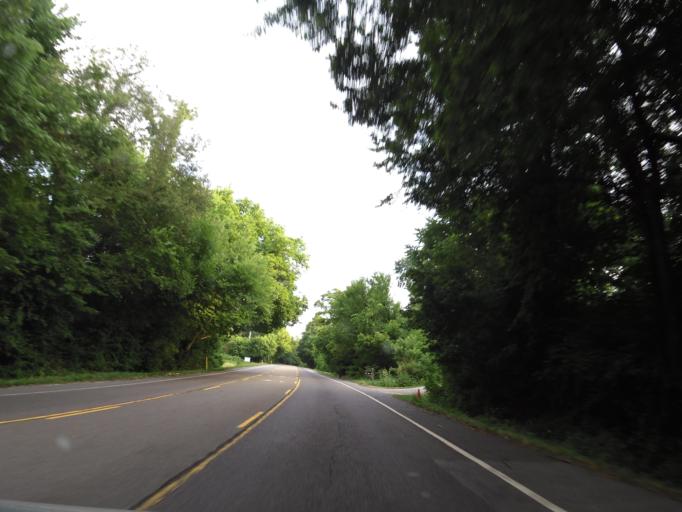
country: US
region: Tennessee
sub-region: Knox County
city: Knoxville
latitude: 35.9936
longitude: -83.8280
